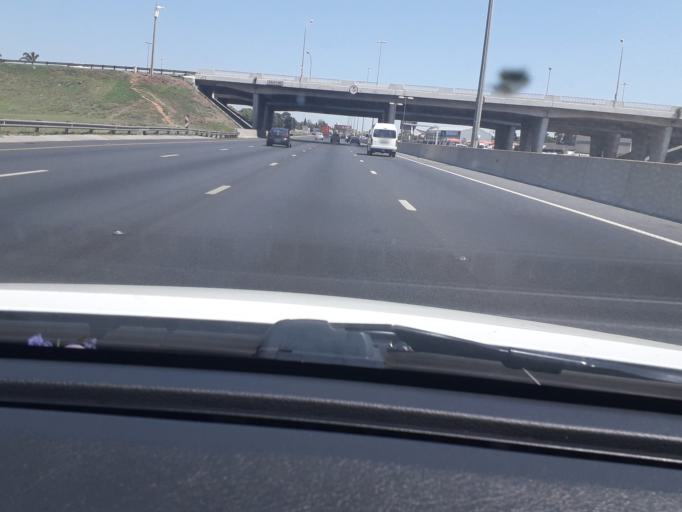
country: ZA
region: Gauteng
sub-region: Ekurhuleni Metropolitan Municipality
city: Germiston
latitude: -26.1764
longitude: 28.1994
